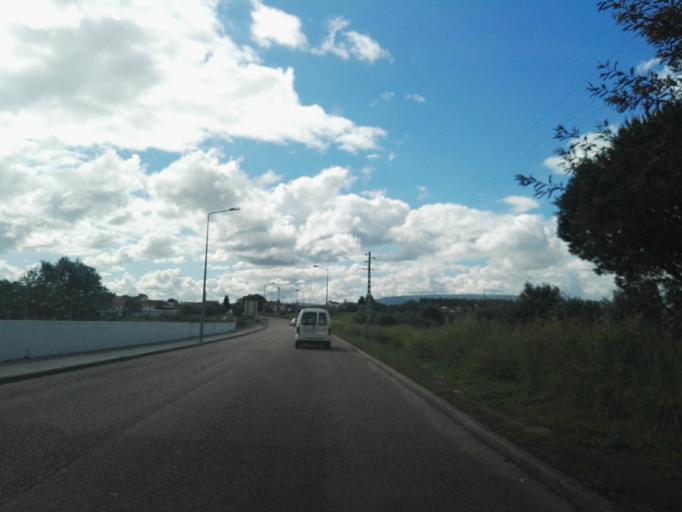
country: PT
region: Santarem
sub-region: Torres Novas
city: Riachos
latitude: 39.4471
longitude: -8.5080
